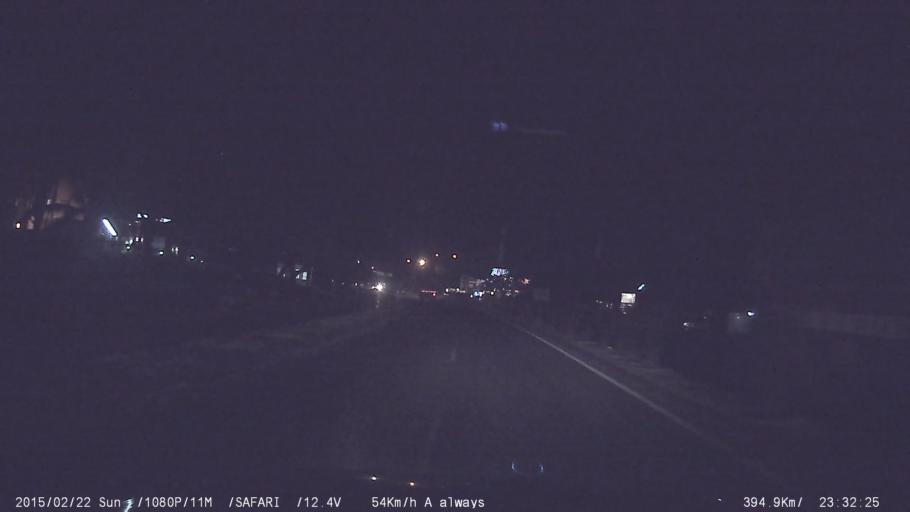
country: IN
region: Tamil Nadu
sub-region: Salem
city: Salem
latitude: 11.6784
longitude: 78.1281
